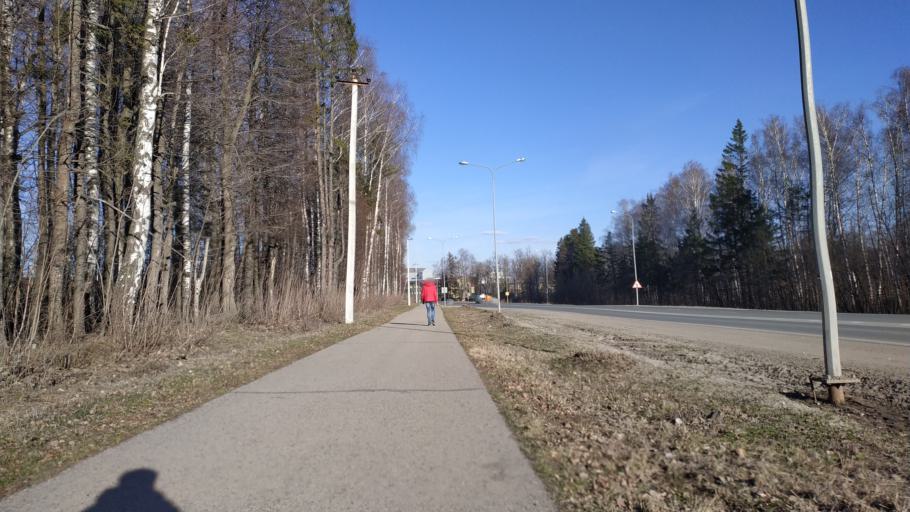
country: RU
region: Chuvashia
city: Novyye Lapsary
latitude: 56.1300
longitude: 47.1565
